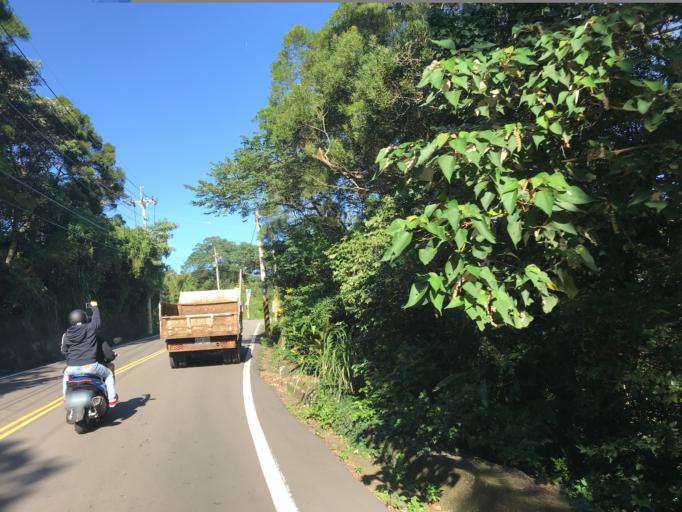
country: TW
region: Taiwan
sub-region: Hsinchu
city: Zhubei
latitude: 24.8646
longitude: 121.0951
